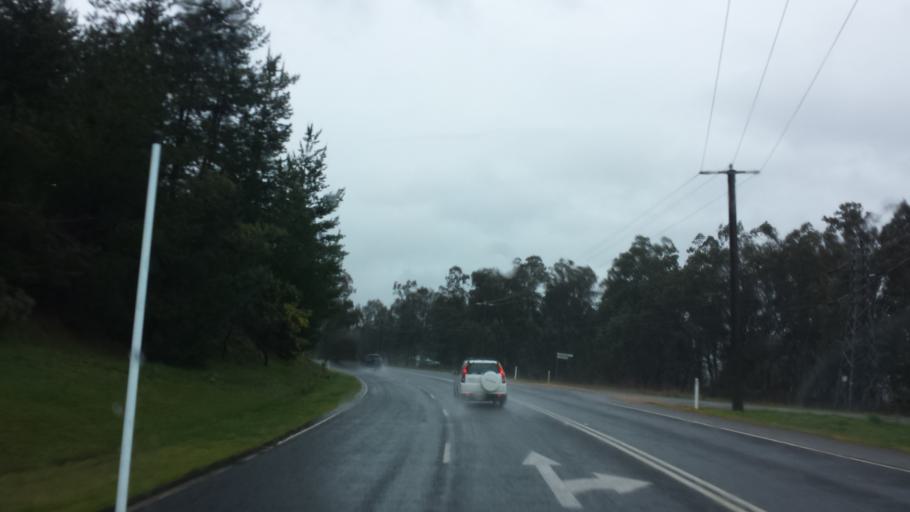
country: AU
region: Victoria
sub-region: Alpine
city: Mount Beauty
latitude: -36.5813
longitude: 146.7512
